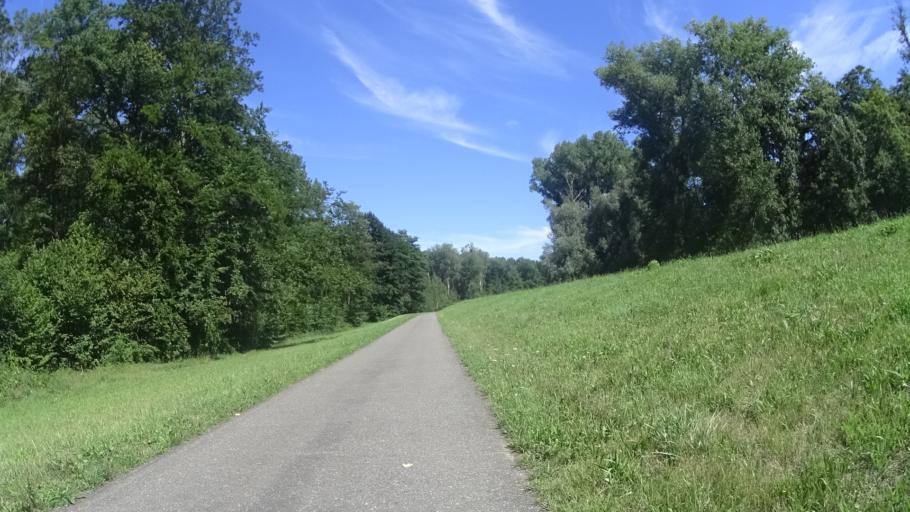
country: DE
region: Rheinland-Pfalz
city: Leimersheim
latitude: 49.1482
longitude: 8.3641
